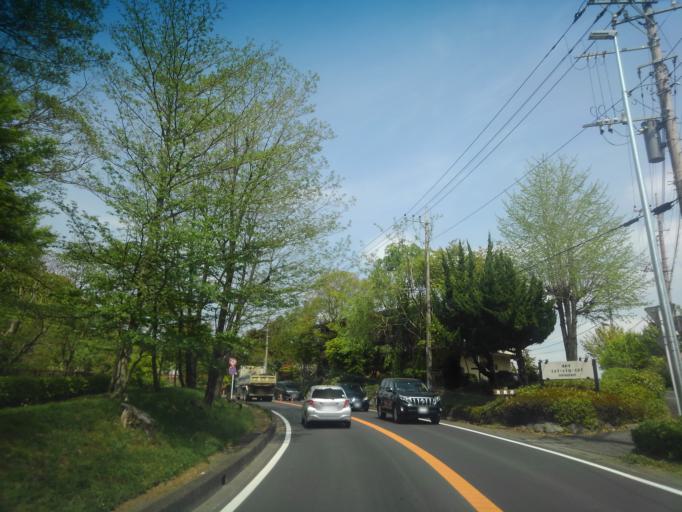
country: JP
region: Tokyo
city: Higashimurayama-shi
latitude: 35.7669
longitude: 139.4161
